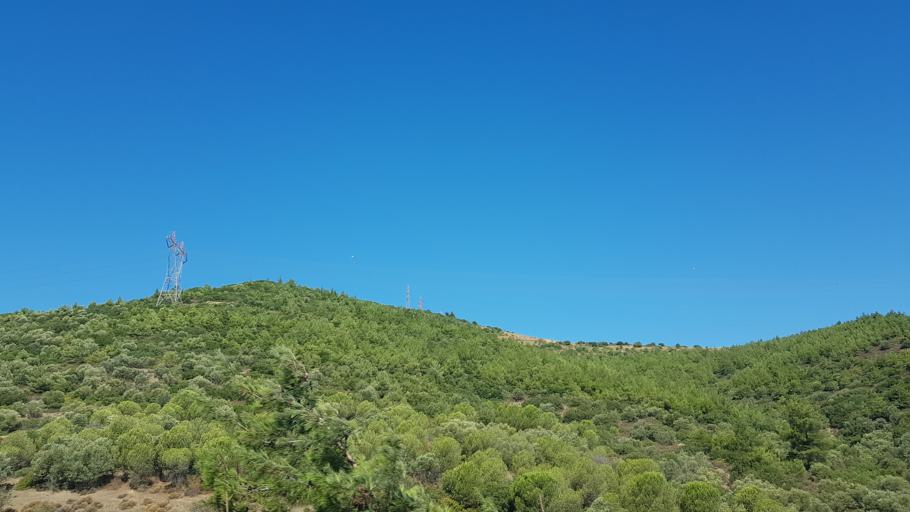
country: TR
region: Izmir
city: Buca
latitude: 38.4046
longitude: 27.2318
